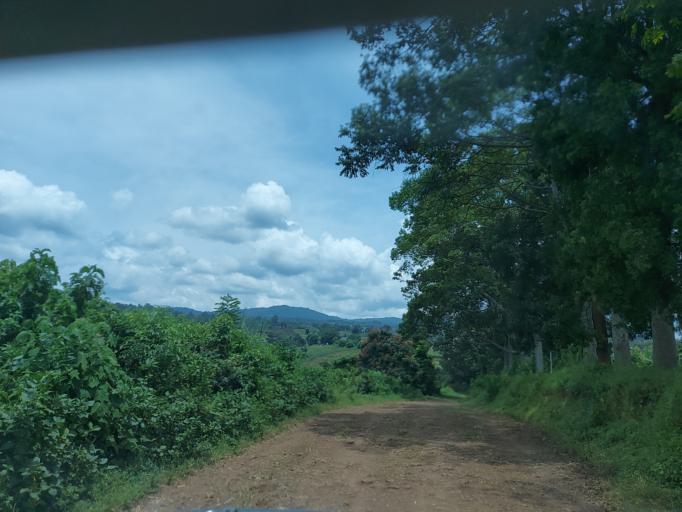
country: CD
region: South Kivu
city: Kabare
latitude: -2.3379
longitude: 28.7862
